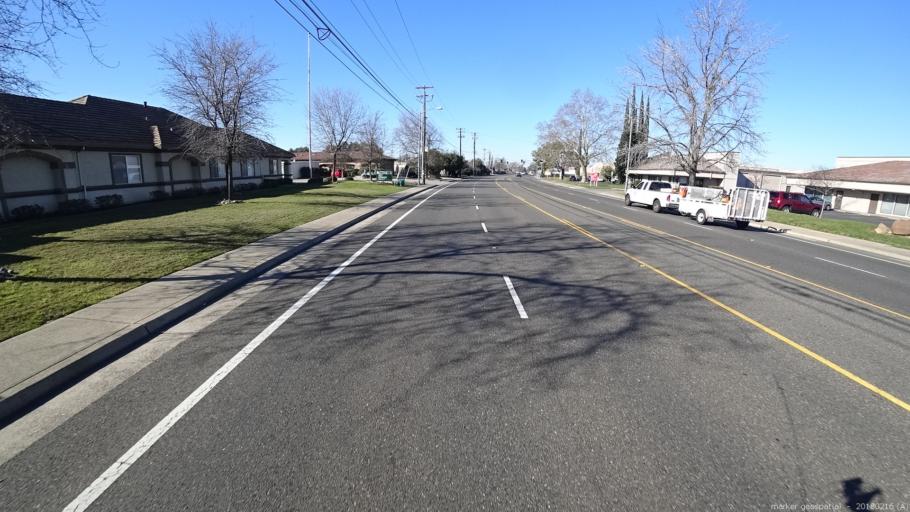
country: US
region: California
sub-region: Sacramento County
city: Gold River
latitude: 38.6190
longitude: -121.2641
